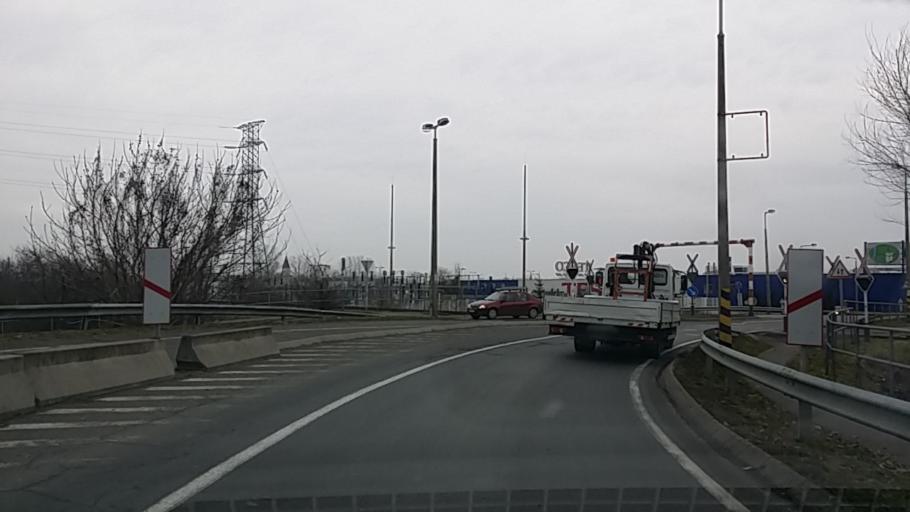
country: HU
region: Bacs-Kiskun
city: Baja
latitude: 46.1926
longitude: 18.9334
